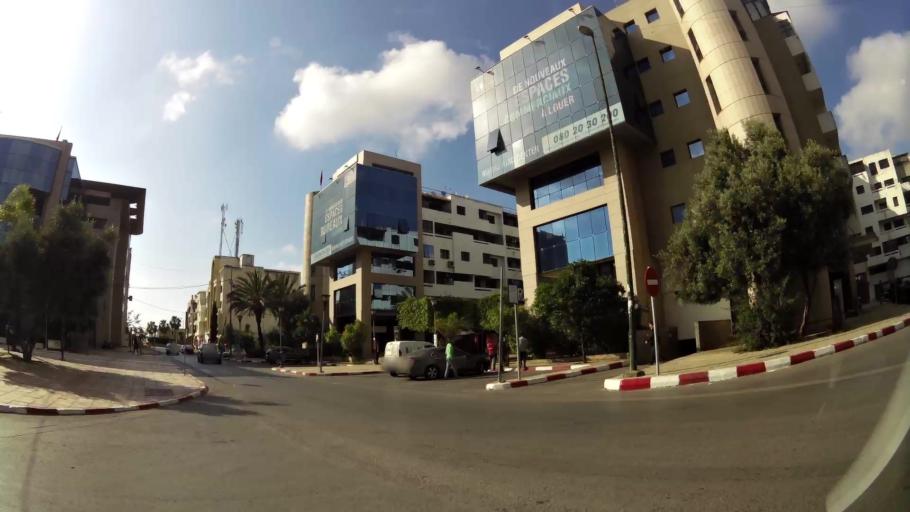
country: MA
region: Rabat-Sale-Zemmour-Zaer
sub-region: Skhirate-Temara
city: Temara
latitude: 33.9596
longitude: -6.8681
